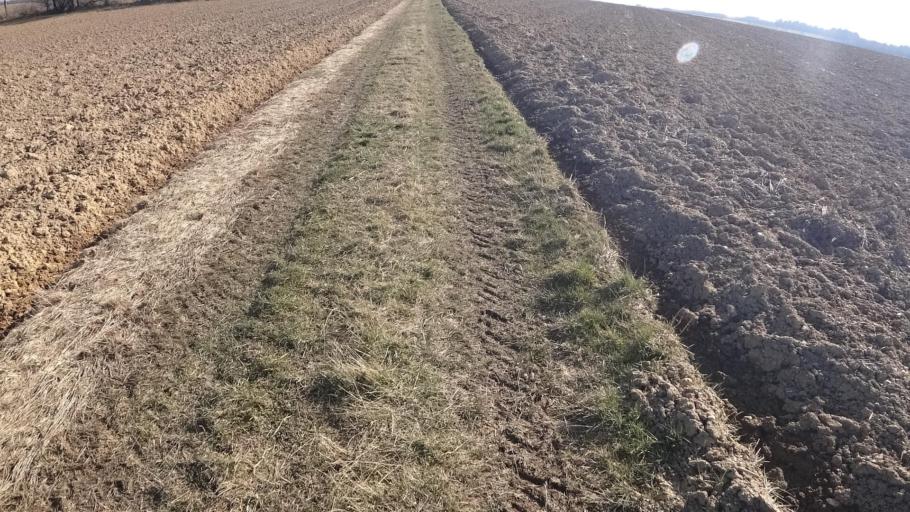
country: DE
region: Rheinland-Pfalz
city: Mutterschied
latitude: 49.9888
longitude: 7.5632
